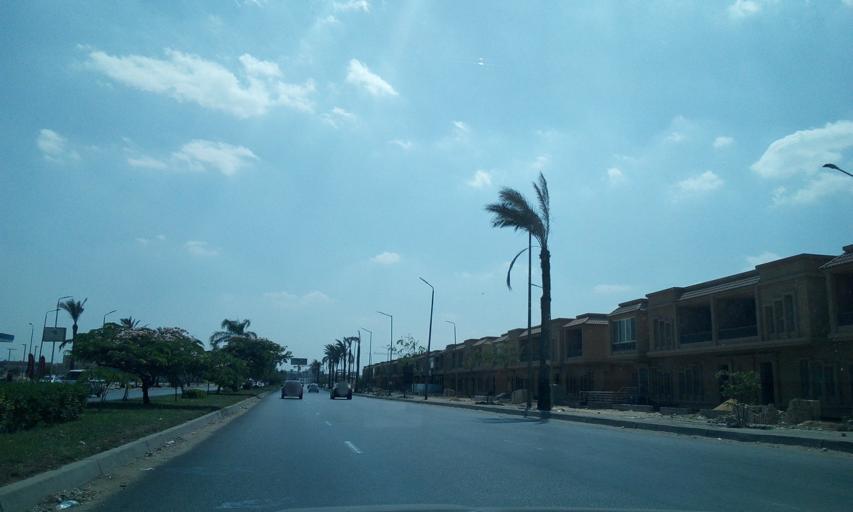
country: EG
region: Muhafazat al Qalyubiyah
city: Al Khankah
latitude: 30.0898
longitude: 31.3690
